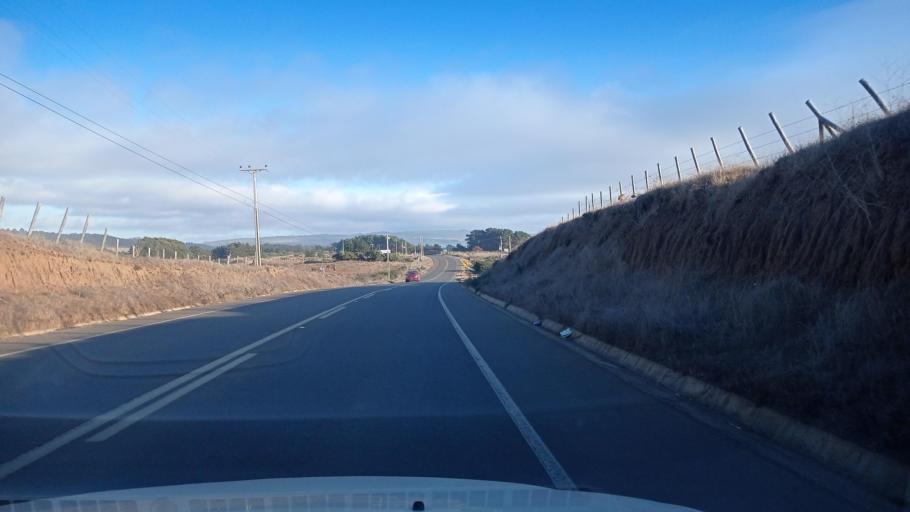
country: CL
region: O'Higgins
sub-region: Provincia de Colchagua
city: Santa Cruz
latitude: -34.4441
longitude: -72.0320
